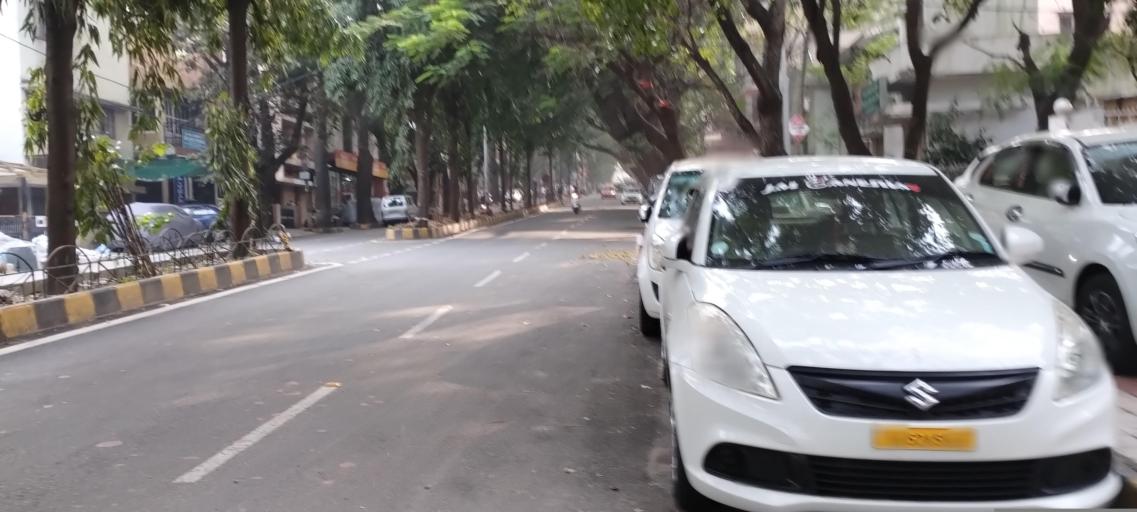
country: IN
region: Karnataka
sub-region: Bangalore Urban
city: Bangalore
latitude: 12.9408
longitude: 77.5440
